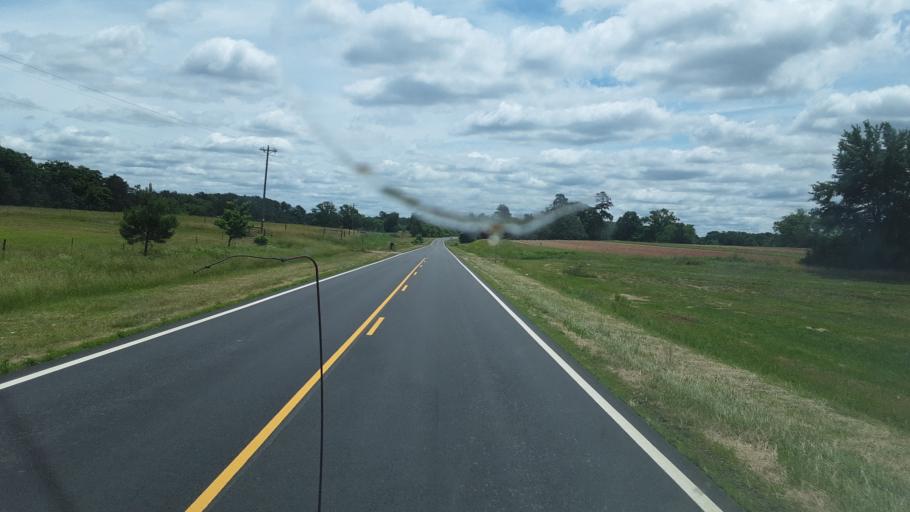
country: US
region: Virginia
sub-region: Pittsylvania County
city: Chatham
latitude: 36.8368
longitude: -79.4550
